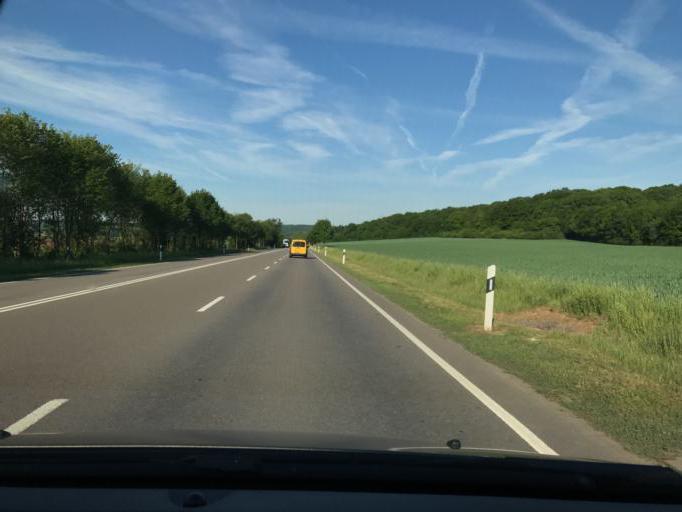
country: LU
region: Luxembourg
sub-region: Canton de Luxembourg
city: Niederanven
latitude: 49.6585
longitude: 6.2846
